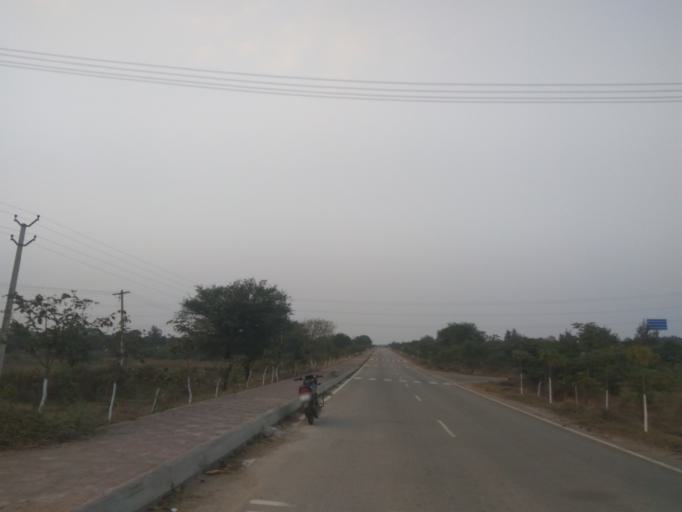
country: IN
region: Telangana
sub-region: Rangareddi
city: Secunderabad
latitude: 17.5480
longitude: 78.6293
